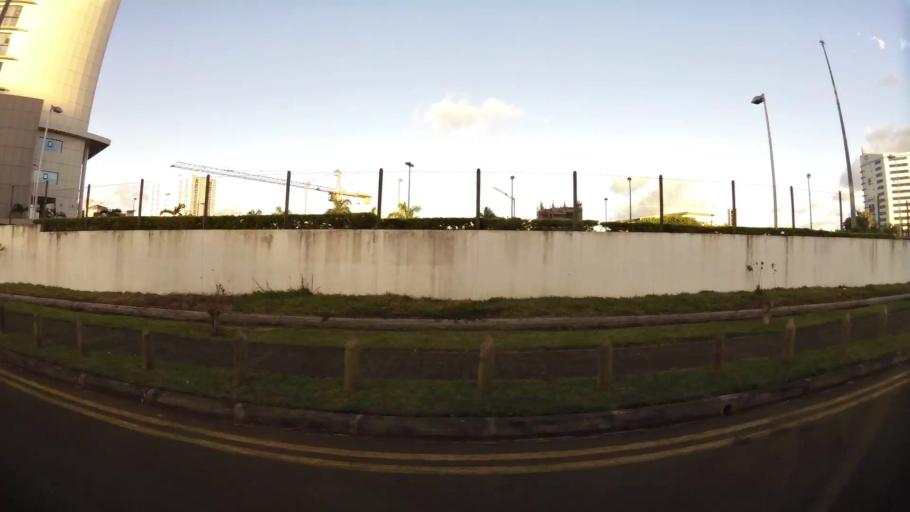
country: MU
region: Plaines Wilhems
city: Ebene
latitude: -20.2453
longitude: 57.4927
